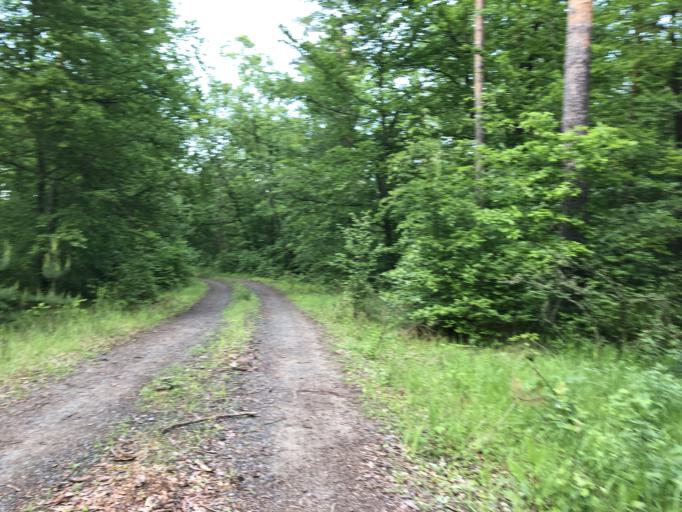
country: DE
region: Bavaria
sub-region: Upper Franconia
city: Memmelsdorf
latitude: 49.9089
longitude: 10.9538
